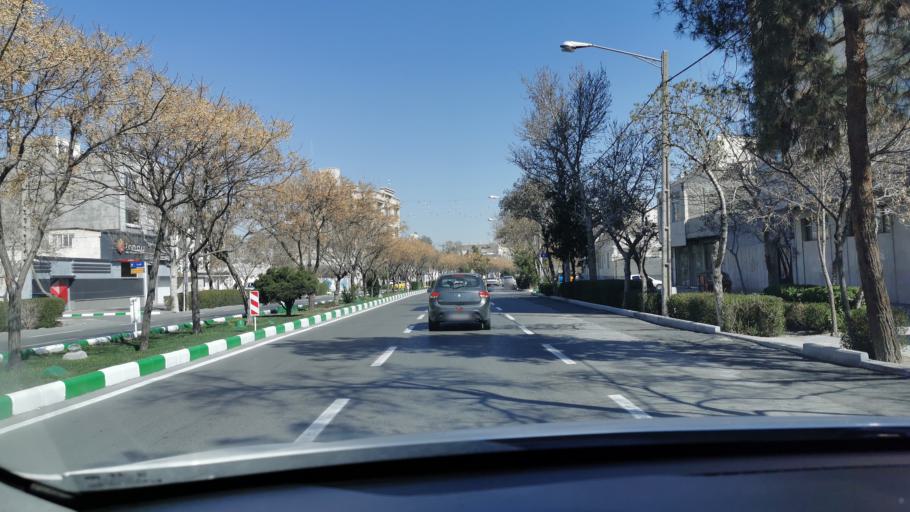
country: IR
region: Razavi Khorasan
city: Mashhad
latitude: 36.2930
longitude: 59.5723
